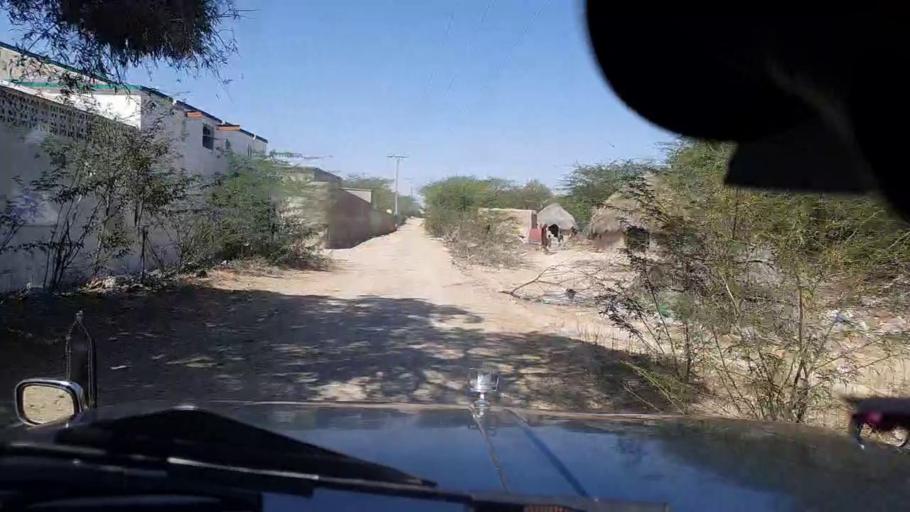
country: PK
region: Sindh
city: Mithi
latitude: 24.5941
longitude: 69.7104
